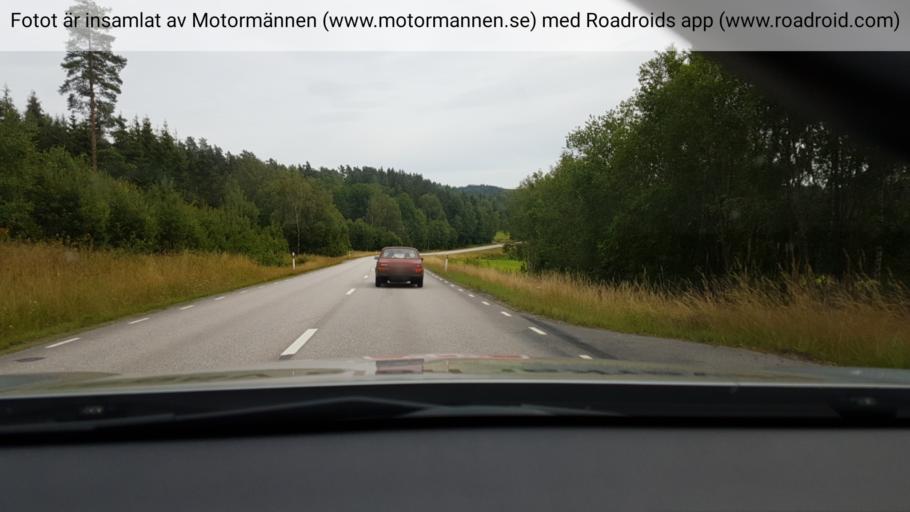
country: SE
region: Vaestra Goetaland
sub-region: Bengtsfors Kommun
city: Billingsfors
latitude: 58.9212
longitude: 12.2202
